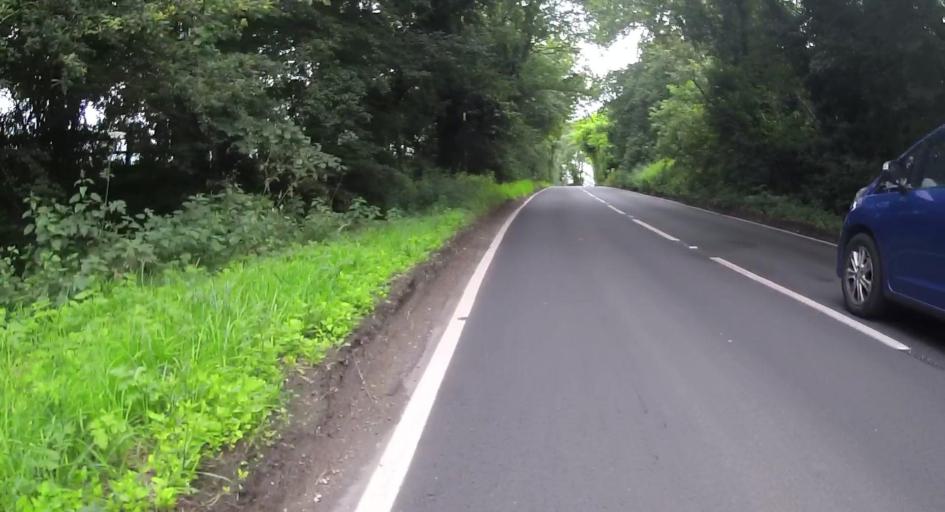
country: GB
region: England
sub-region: Wokingham
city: Barkham
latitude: 51.3914
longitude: -0.8771
